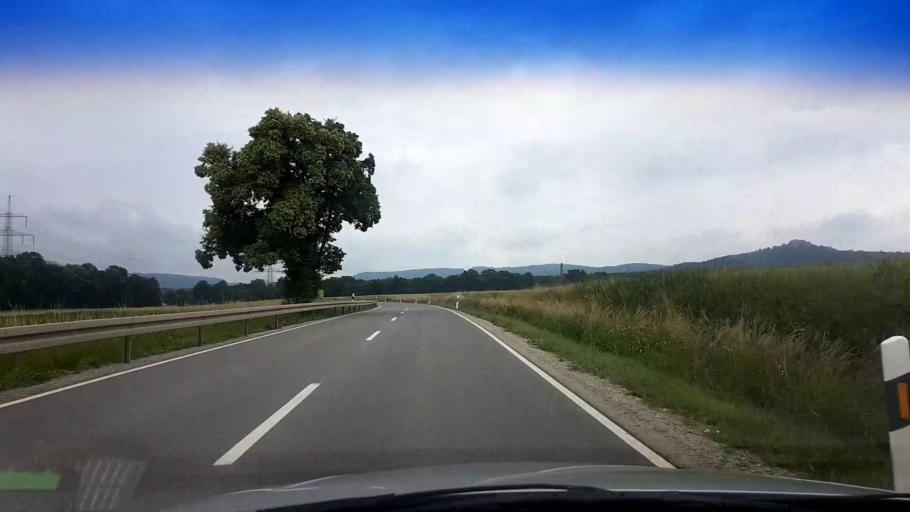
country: DE
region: Bavaria
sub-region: Upper Franconia
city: Schesslitz
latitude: 49.9644
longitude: 11.0142
